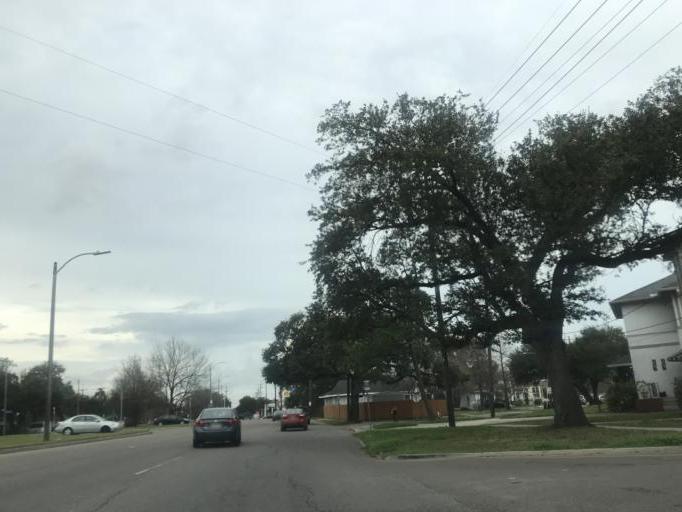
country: US
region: Louisiana
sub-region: Orleans Parish
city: New Orleans
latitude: 29.9441
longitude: -90.1129
